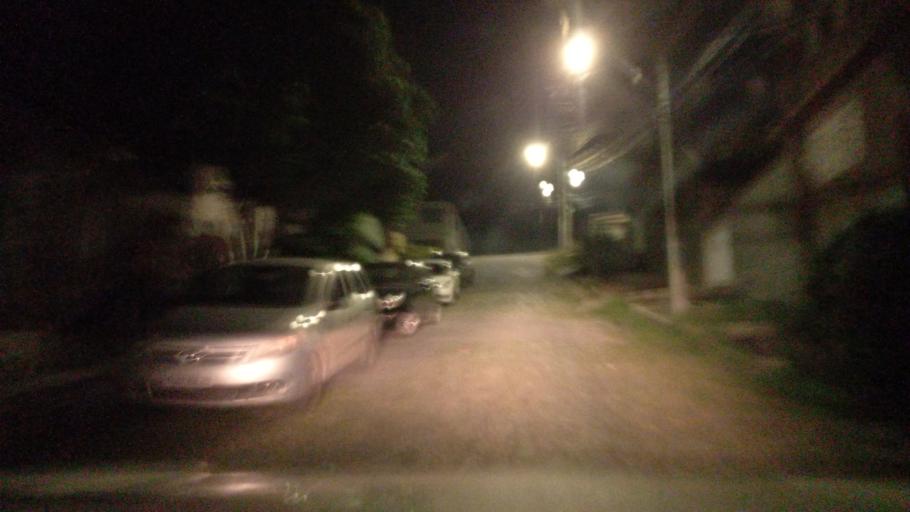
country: BR
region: Minas Gerais
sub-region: Belo Horizonte
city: Belo Horizonte
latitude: -19.8793
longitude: -43.9436
